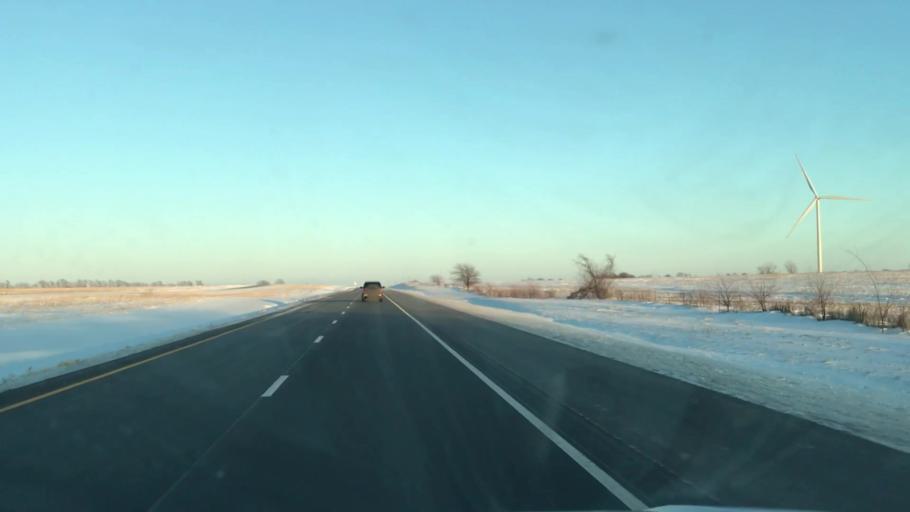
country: US
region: Missouri
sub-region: DeKalb County
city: Maysville
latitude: 39.7615
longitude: -94.3818
